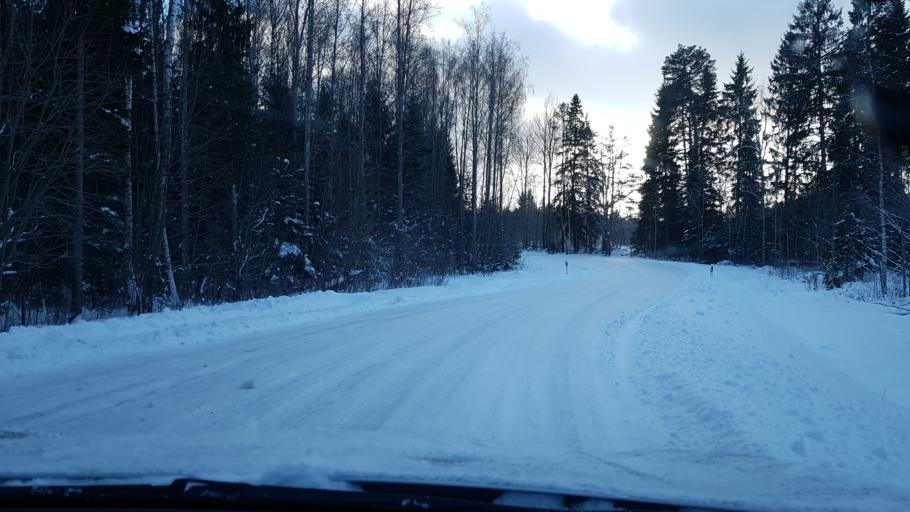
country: EE
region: Harju
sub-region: Nissi vald
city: Turba
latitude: 59.1504
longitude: 24.1515
